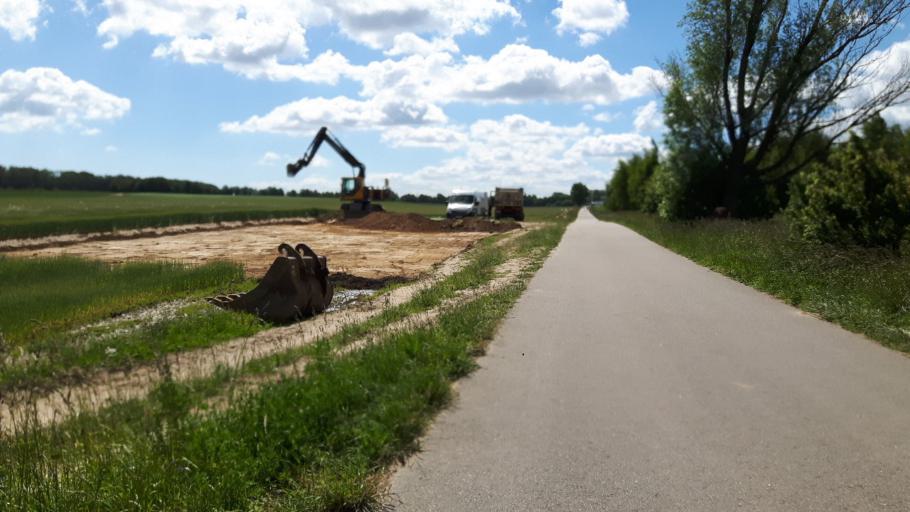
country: PL
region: Pomeranian Voivodeship
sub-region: Gdynia
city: Pogorze
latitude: 54.5709
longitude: 18.5005
